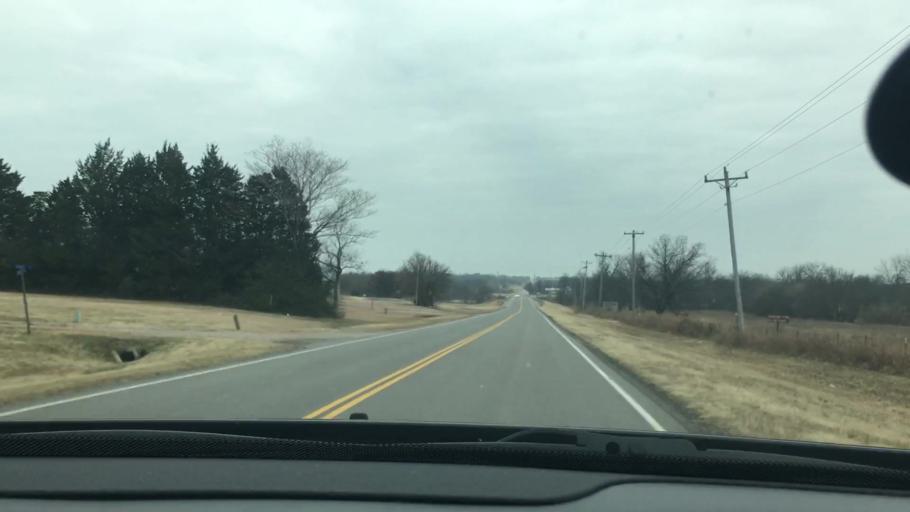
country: US
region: Oklahoma
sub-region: Carter County
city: Healdton
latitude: 34.2510
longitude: -97.4923
